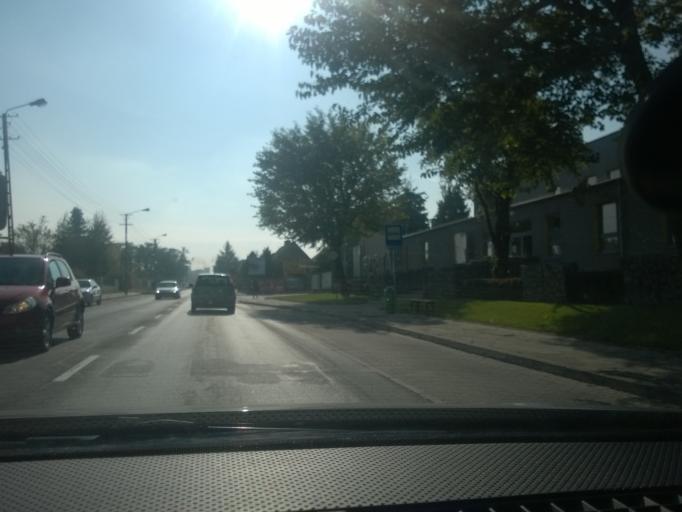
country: PL
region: Greater Poland Voivodeship
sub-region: Kalisz
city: Kalisz
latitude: 51.7463
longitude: 18.0964
